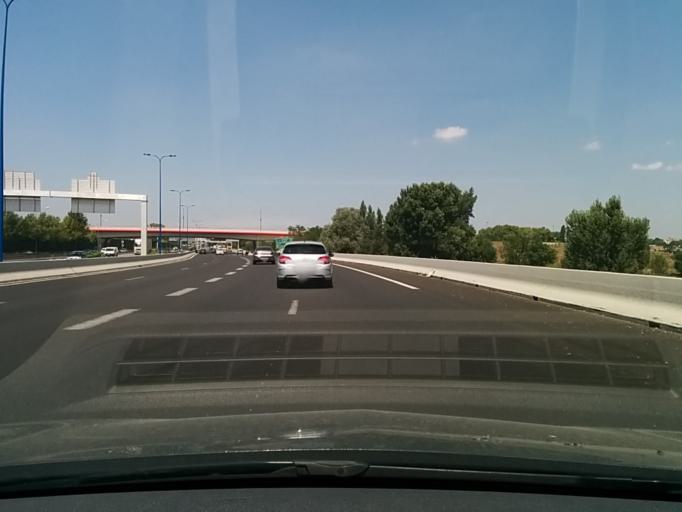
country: FR
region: Midi-Pyrenees
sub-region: Departement de la Haute-Garonne
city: Ramonville-Saint-Agne
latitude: 43.5621
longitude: 1.4886
